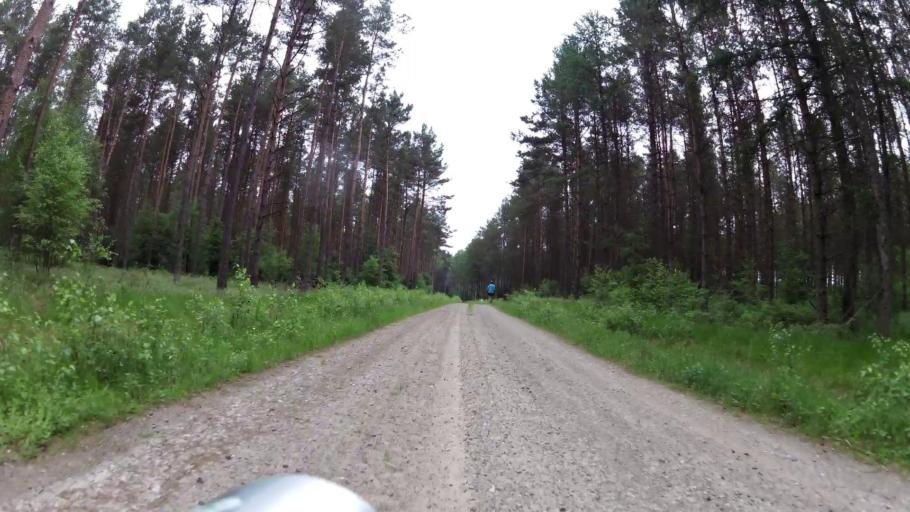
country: PL
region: West Pomeranian Voivodeship
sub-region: Powiat szczecinecki
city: Bialy Bor
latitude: 53.9281
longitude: 16.8357
